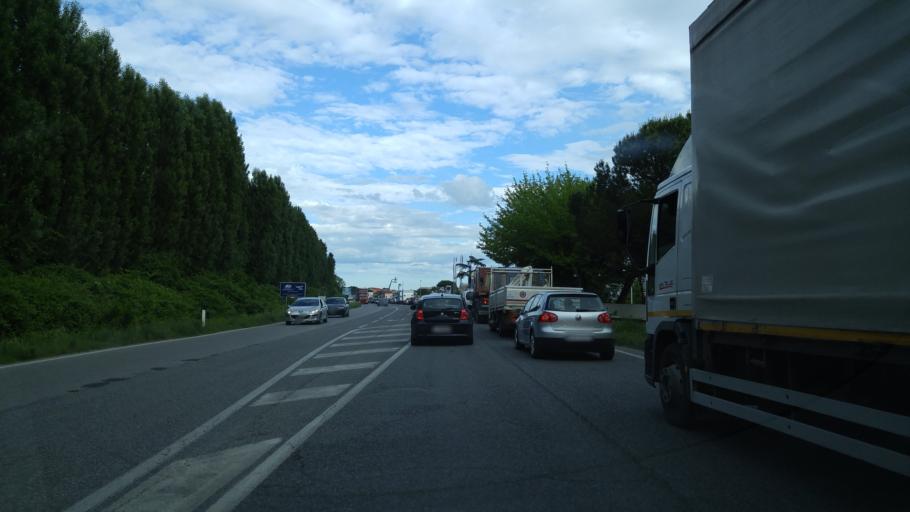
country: IT
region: Emilia-Romagna
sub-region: Provincia di Rimini
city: Rimini
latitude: 44.0429
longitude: 12.5645
